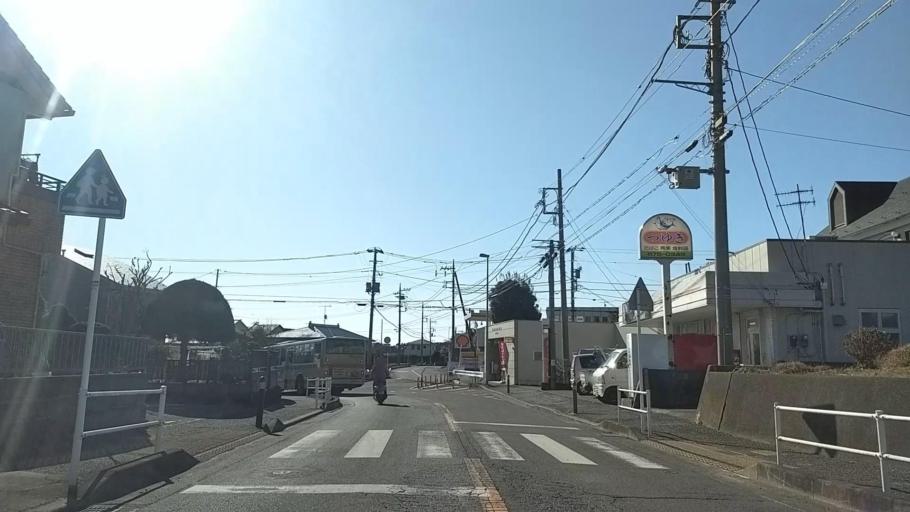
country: JP
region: Kanagawa
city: Hadano
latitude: 35.3996
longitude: 139.1937
